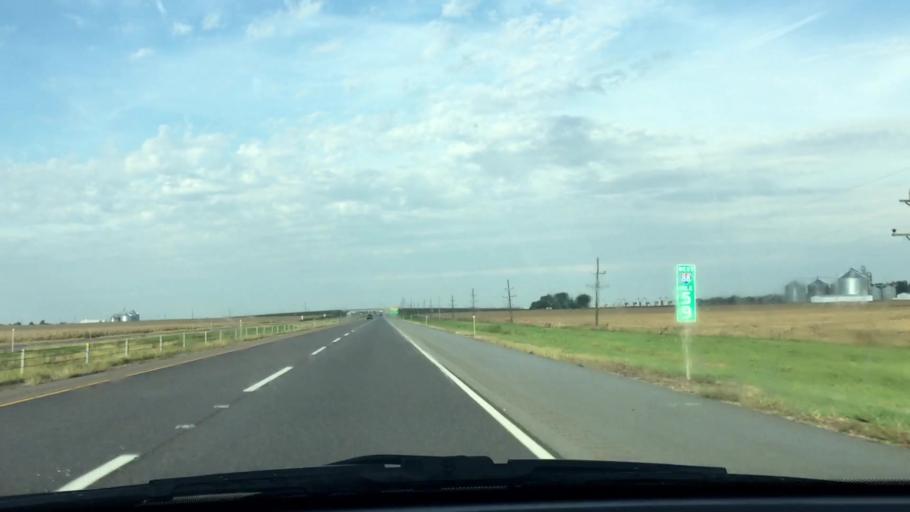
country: US
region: Illinois
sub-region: Lee County
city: Franklin Grove
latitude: 41.8231
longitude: -89.3759
